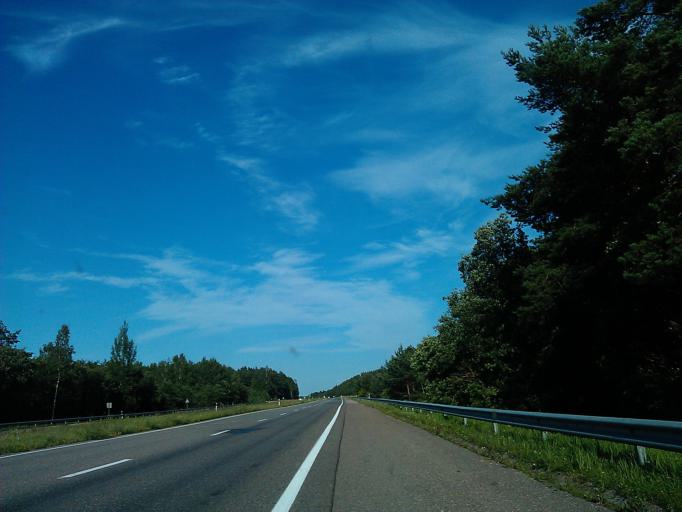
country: LV
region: Incukalns
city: Incukalns
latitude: 57.1286
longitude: 24.7173
